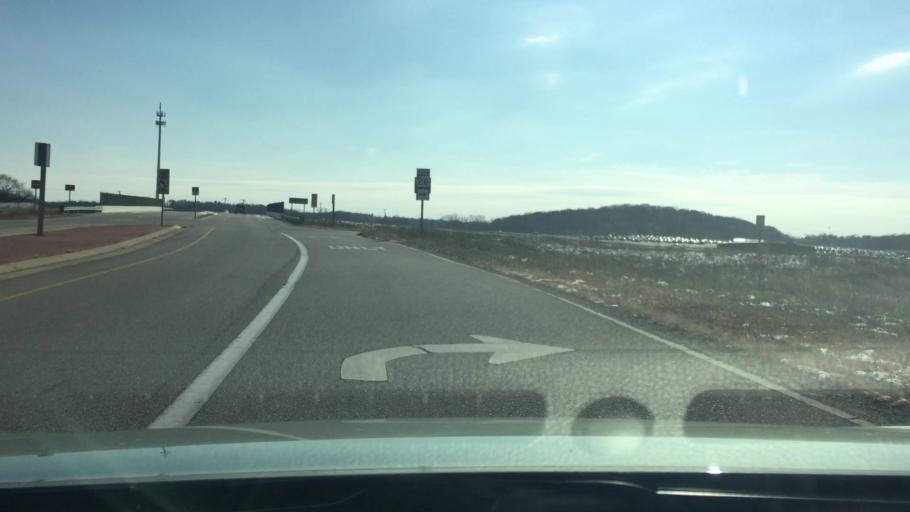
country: US
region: Wisconsin
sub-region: Jefferson County
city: Jefferson
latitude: 43.0354
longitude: -88.8062
